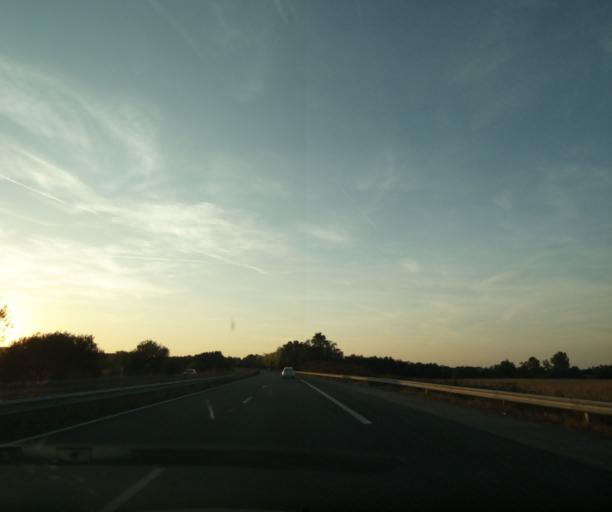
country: FR
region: Aquitaine
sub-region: Departement du Lot-et-Garonne
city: Tonneins
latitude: 44.3738
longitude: 0.2345
